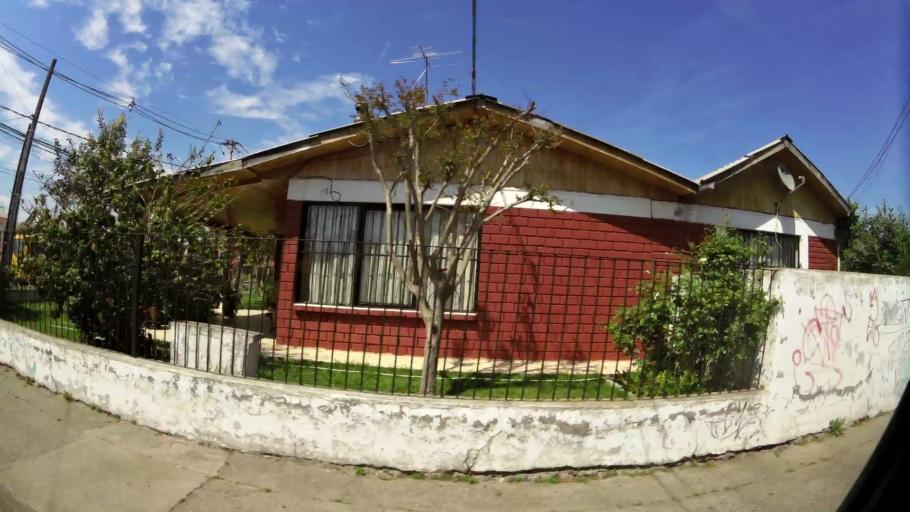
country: CL
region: Santiago Metropolitan
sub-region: Provincia de Talagante
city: Talagante
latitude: -33.6615
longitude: -70.9168
